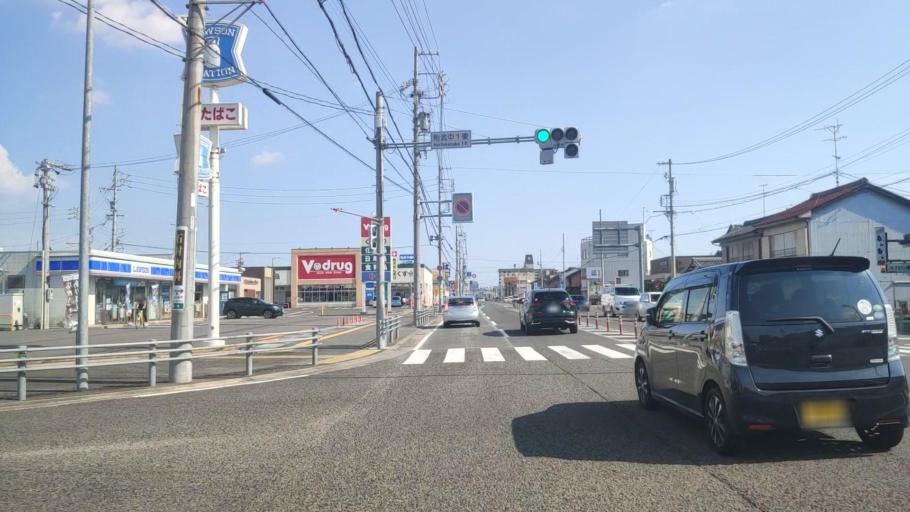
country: JP
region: Gifu
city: Gifu-shi
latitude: 35.4409
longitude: 136.7468
